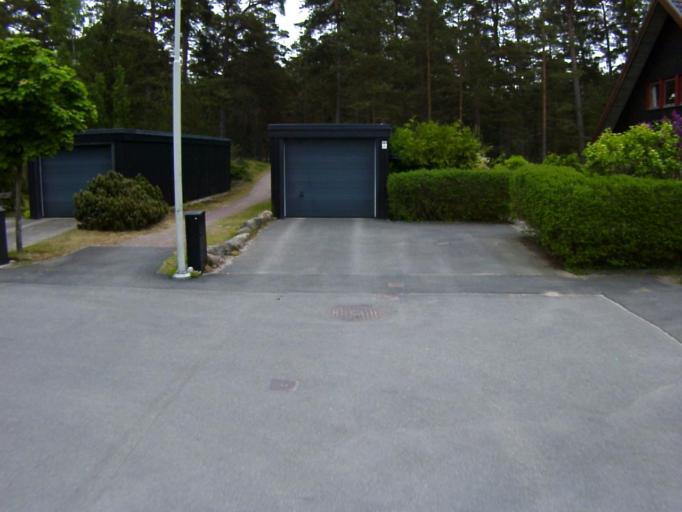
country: SE
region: Skane
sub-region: Kristianstads Kommun
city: Ahus
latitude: 55.9106
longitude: 14.2796
